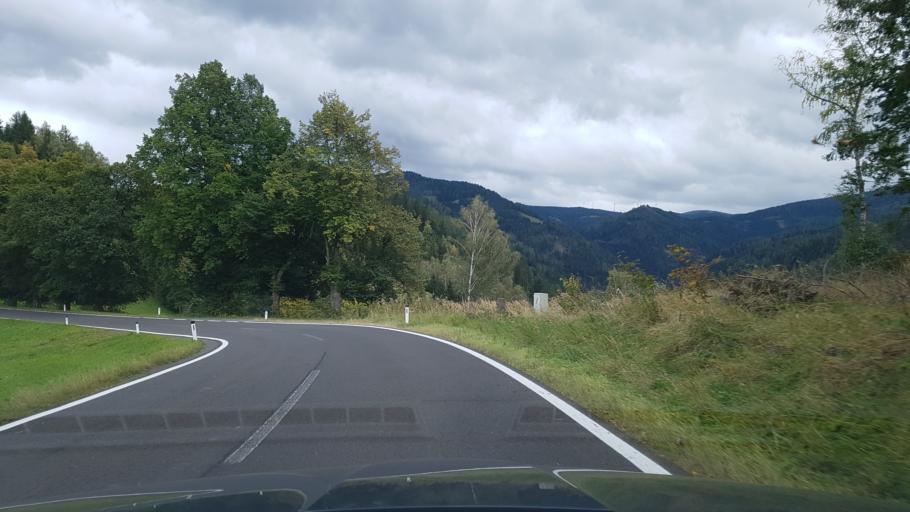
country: AT
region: Styria
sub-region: Politischer Bezirk Murtal
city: Kleinlobming
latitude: 47.1360
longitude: 14.8535
